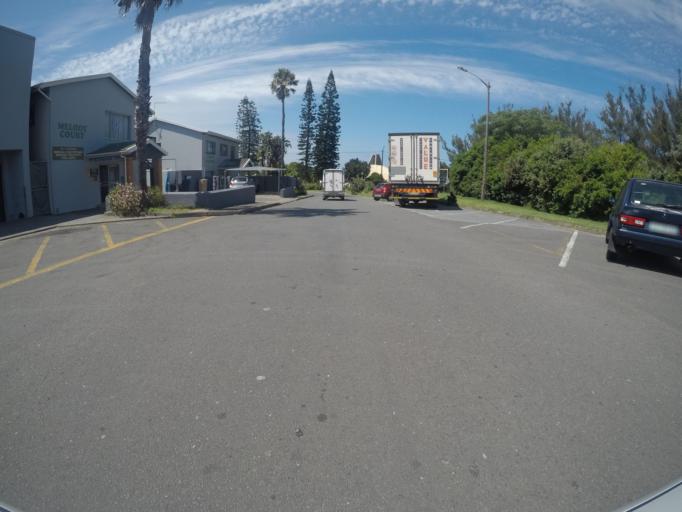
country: ZA
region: Eastern Cape
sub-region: Buffalo City Metropolitan Municipality
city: East London
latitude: -32.9409
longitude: 28.0230
